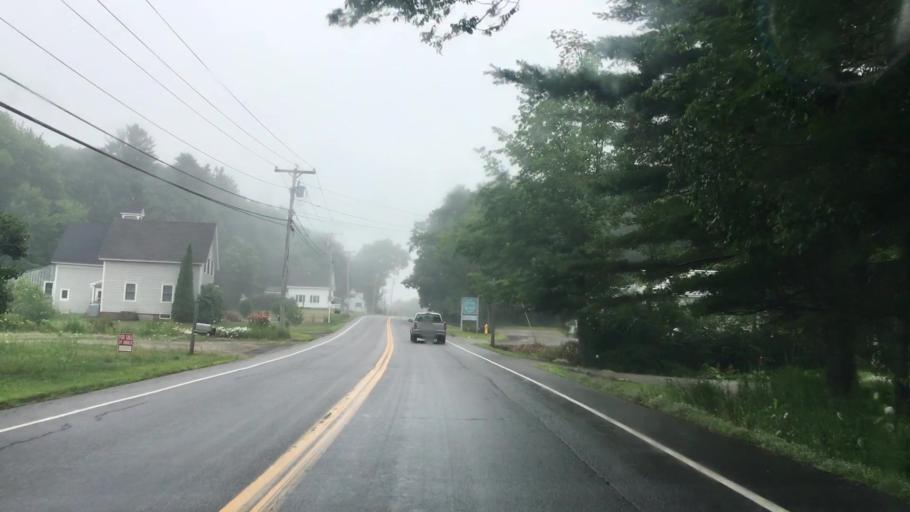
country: US
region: Maine
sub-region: Lincoln County
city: Boothbay
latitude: 43.8825
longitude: -69.6318
